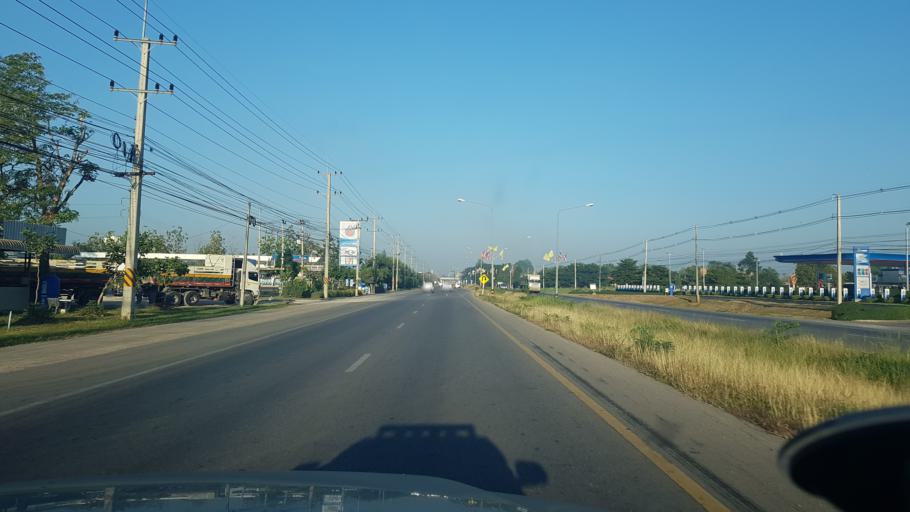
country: TH
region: Khon Kaen
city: Chum Phae
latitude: 16.5831
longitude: 102.0130
